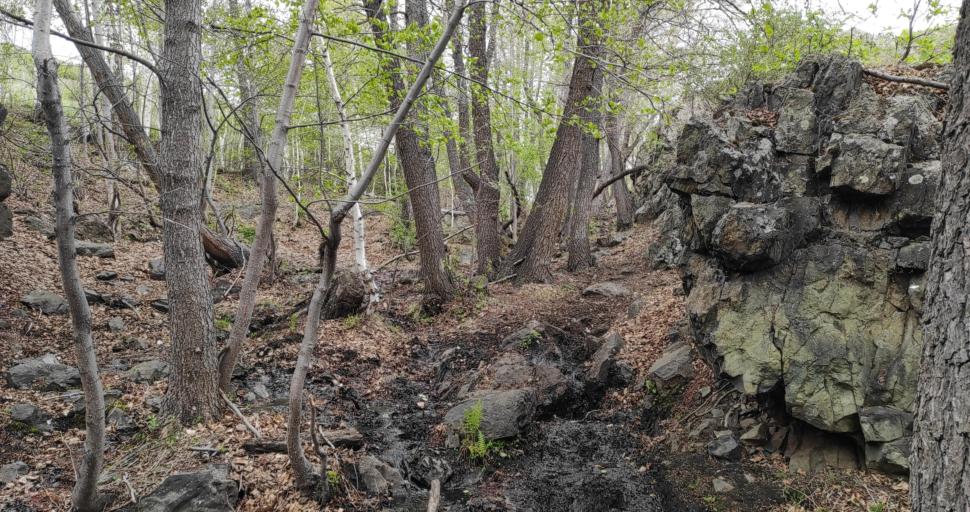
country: RU
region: Bashkortostan
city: Sibay
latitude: 52.7197
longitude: 58.5397
